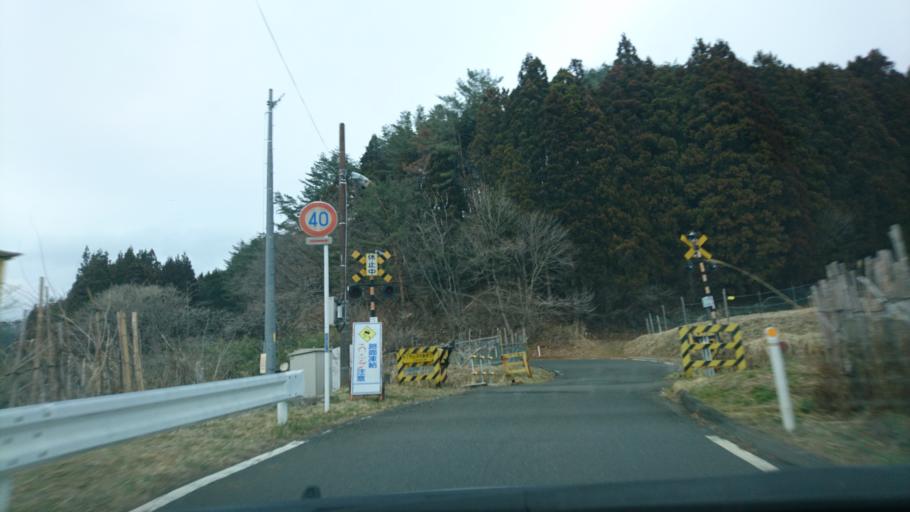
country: JP
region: Iwate
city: Ofunato
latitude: 38.9863
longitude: 141.5531
